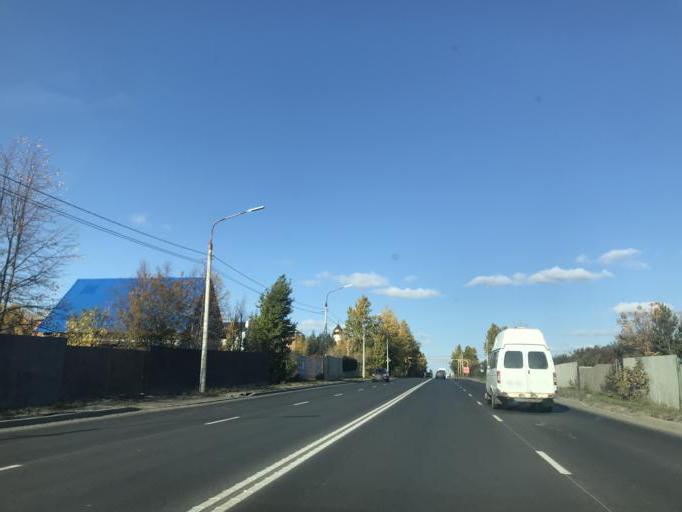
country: RU
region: Chelyabinsk
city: Roshchino
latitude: 55.2365
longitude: 61.3173
